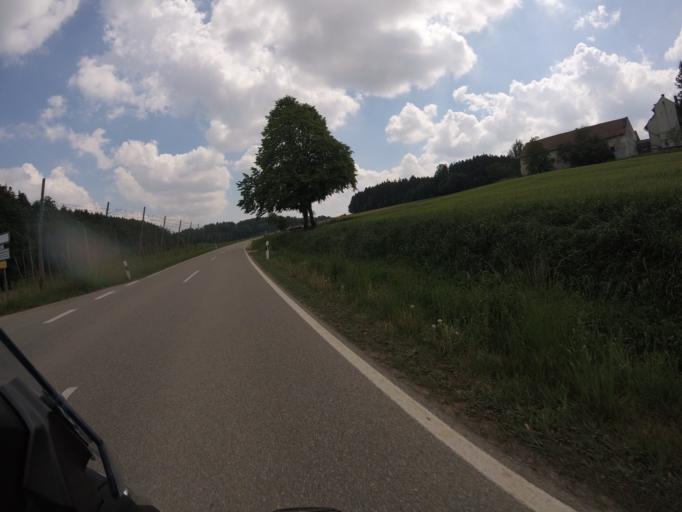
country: DE
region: Bavaria
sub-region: Lower Bavaria
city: Mainburg
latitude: 48.6256
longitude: 11.8161
